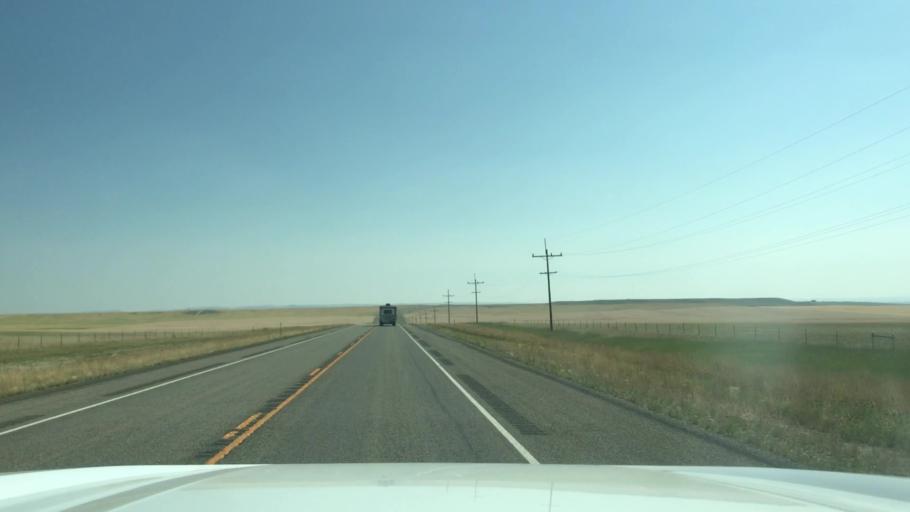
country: US
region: Montana
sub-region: Wheatland County
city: Harlowton
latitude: 46.4953
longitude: -109.7661
